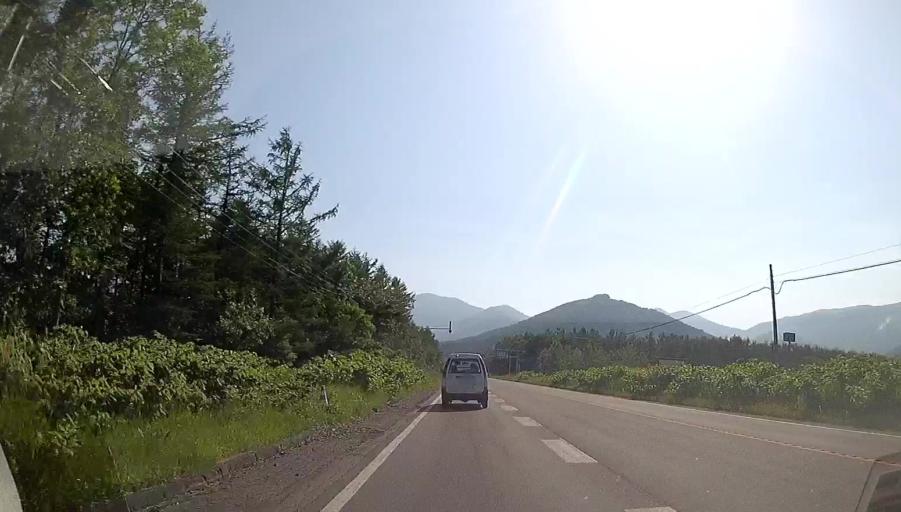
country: JP
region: Hokkaido
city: Otofuke
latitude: 42.9756
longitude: 142.8219
